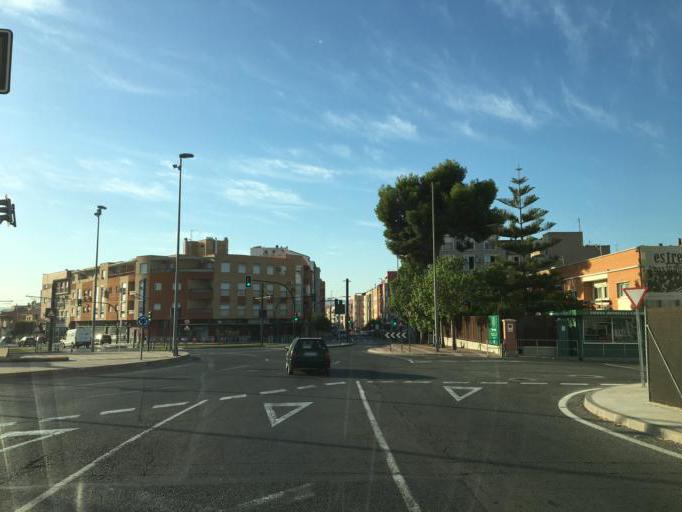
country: ES
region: Murcia
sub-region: Murcia
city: Murcia
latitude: 38.0141
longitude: -1.1570
